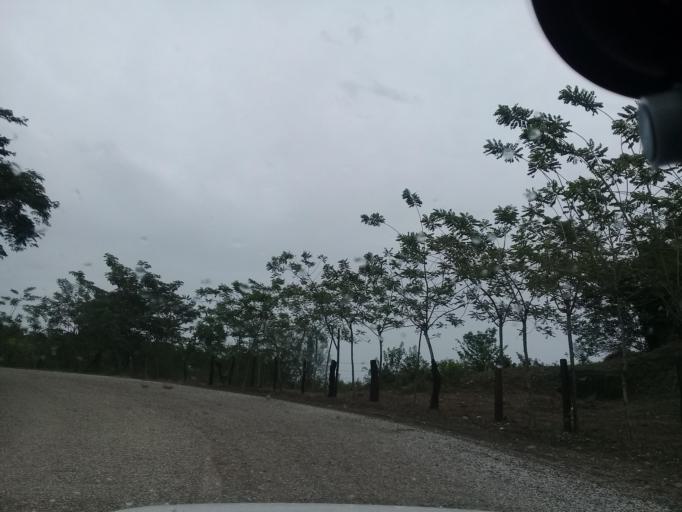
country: MX
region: Veracruz
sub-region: Chalma
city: San Pedro Coyutla
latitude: 21.2119
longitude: -98.3827
